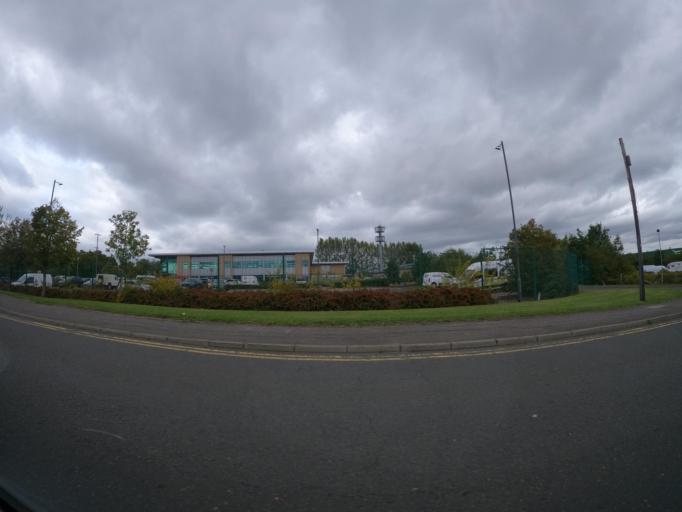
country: GB
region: Scotland
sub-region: Midlothian
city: Loanhead
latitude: 55.8736
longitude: -3.1674
